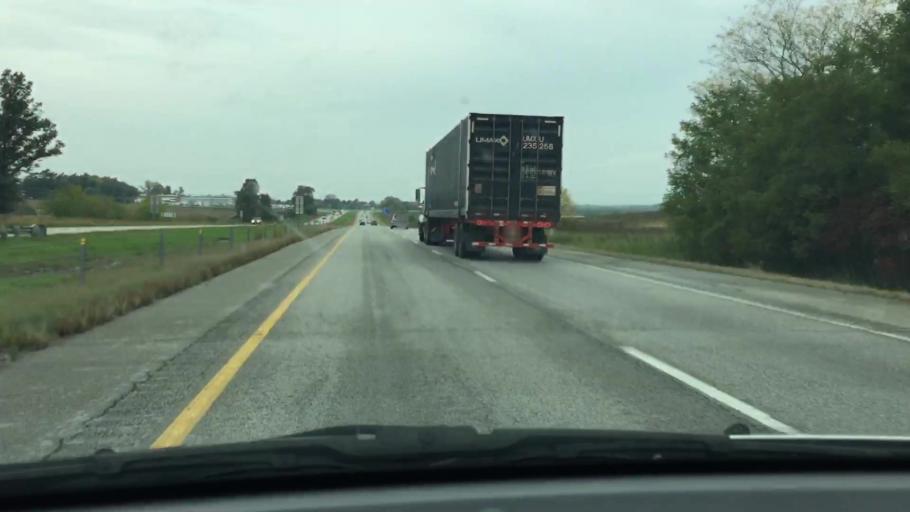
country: US
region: Iowa
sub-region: Johnson County
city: Tiffin
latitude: 41.6944
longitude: -91.6472
